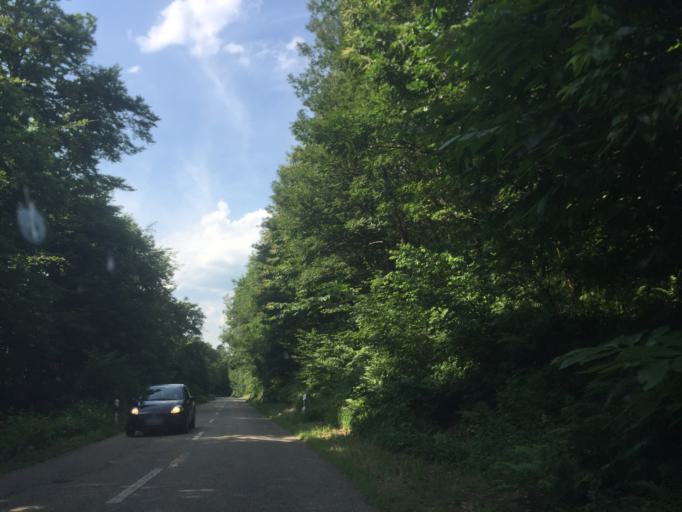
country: DE
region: Baden-Wuerttemberg
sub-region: Karlsruhe Region
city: Heidelberg
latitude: 49.3935
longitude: 8.7143
